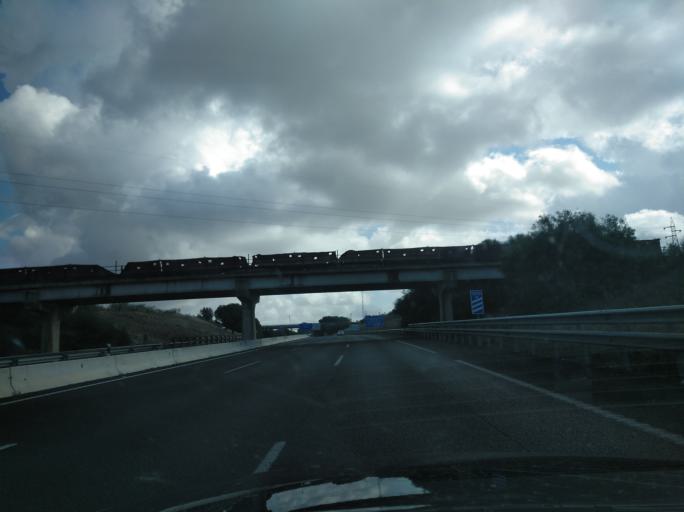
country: ES
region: Andalusia
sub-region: Provincia de Sevilla
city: Benacazon
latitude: 37.3626
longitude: -6.2071
